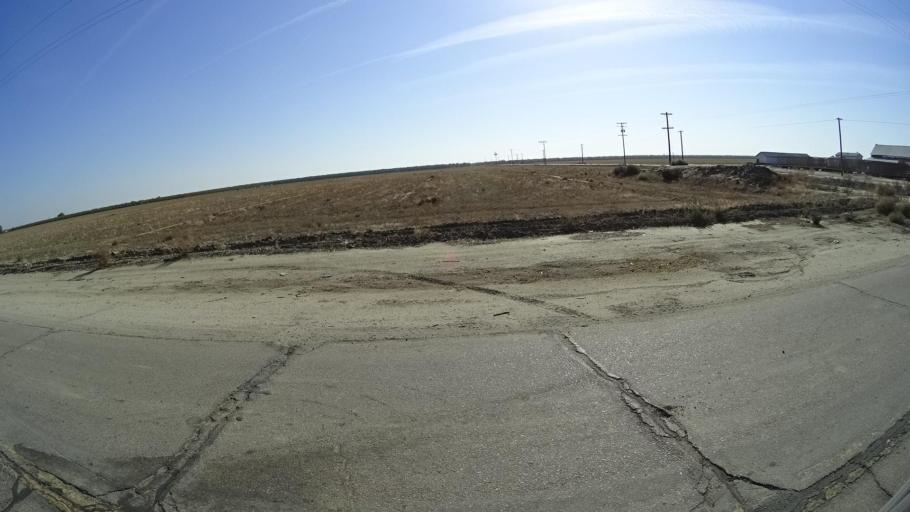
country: US
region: California
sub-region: Kern County
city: Wasco
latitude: 35.6670
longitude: -119.3834
